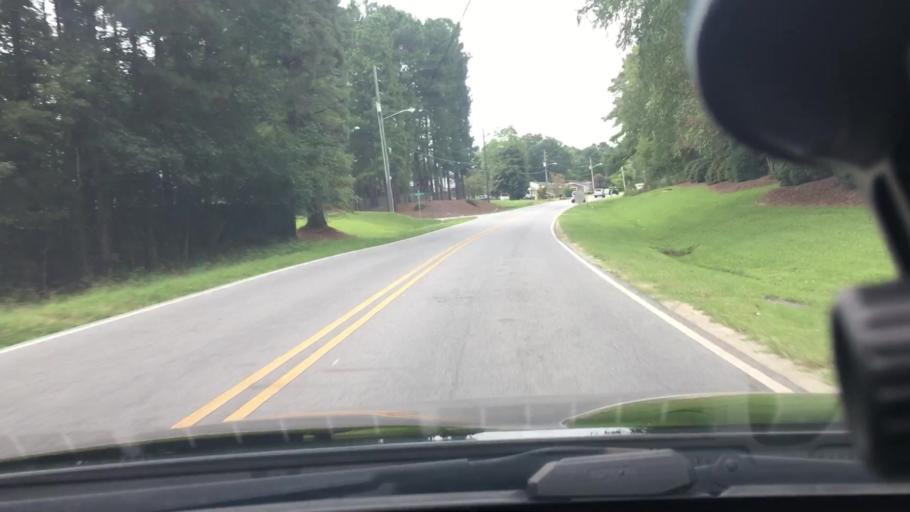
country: US
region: North Carolina
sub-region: Pitt County
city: Windsor
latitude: 35.5728
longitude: -77.3422
